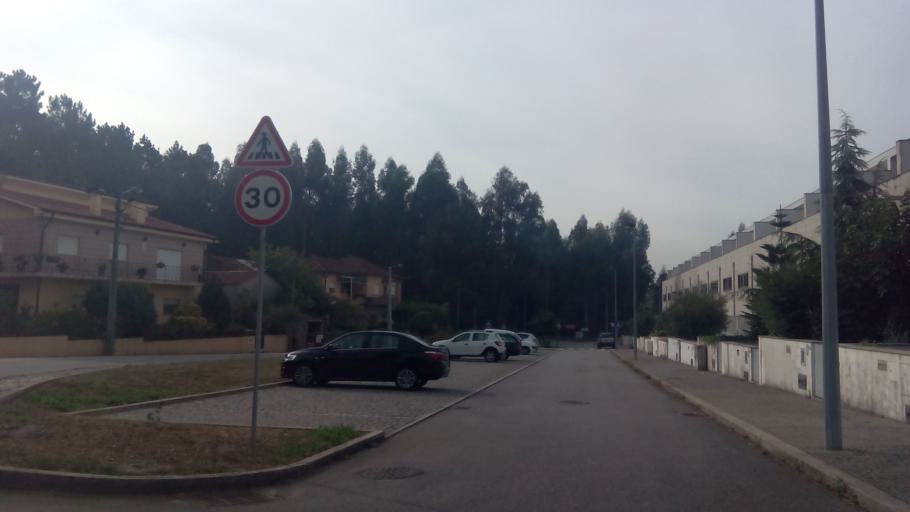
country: PT
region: Porto
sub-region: Paredes
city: Gandra
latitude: 41.1886
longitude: -8.4253
